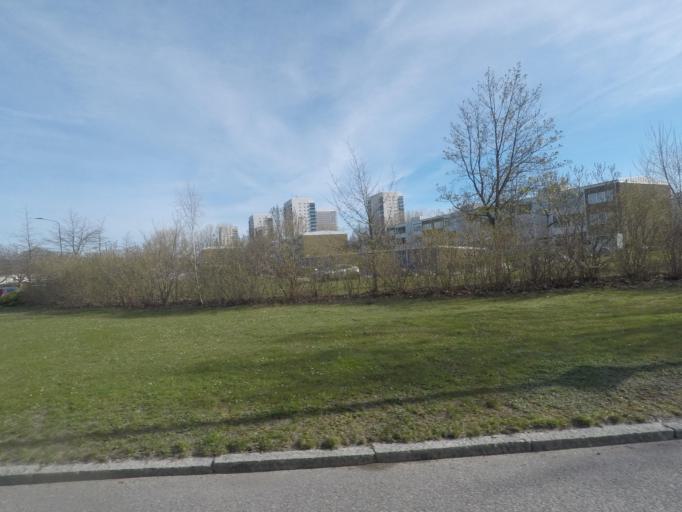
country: SE
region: Skane
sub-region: Malmo
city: Tygelsjo
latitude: 55.5572
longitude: 13.0048
